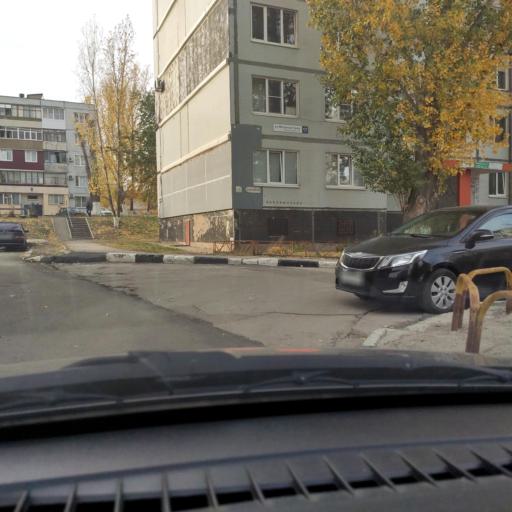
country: RU
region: Samara
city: Zhigulevsk
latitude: 53.4794
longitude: 49.4570
